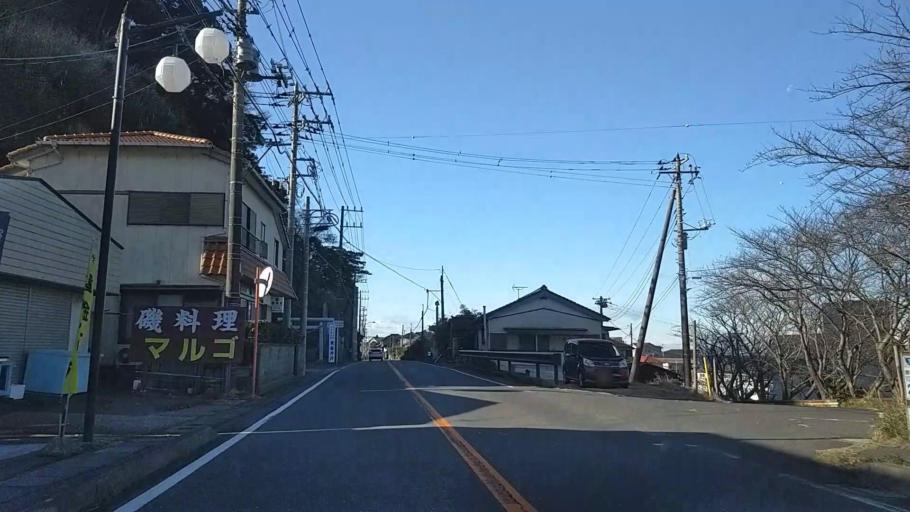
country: JP
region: Chiba
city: Futtsu
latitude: 35.1982
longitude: 139.8277
